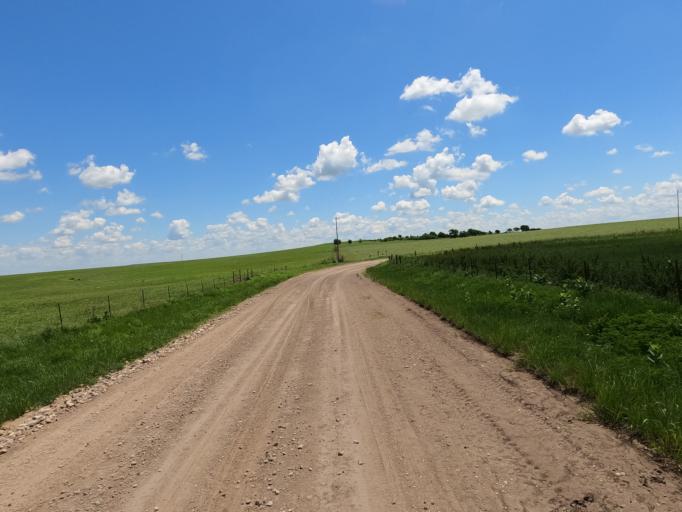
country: US
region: Kansas
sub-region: Marion County
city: Marion
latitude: 38.2310
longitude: -96.7870
